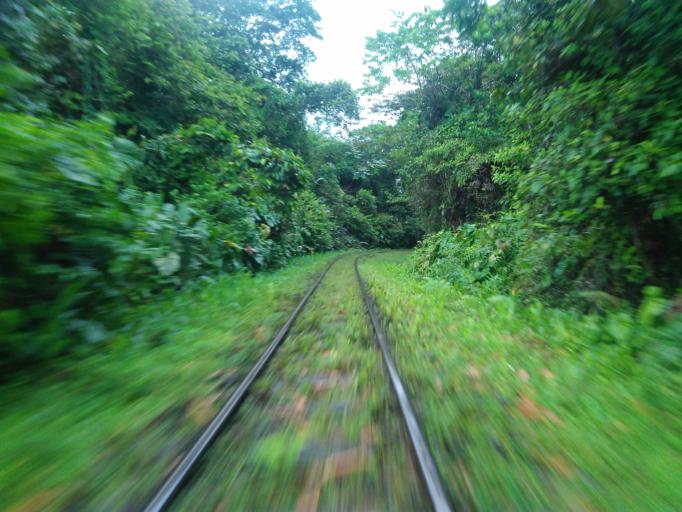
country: CO
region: Valle del Cauca
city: Buenaventura
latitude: 3.8441
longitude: -76.8776
